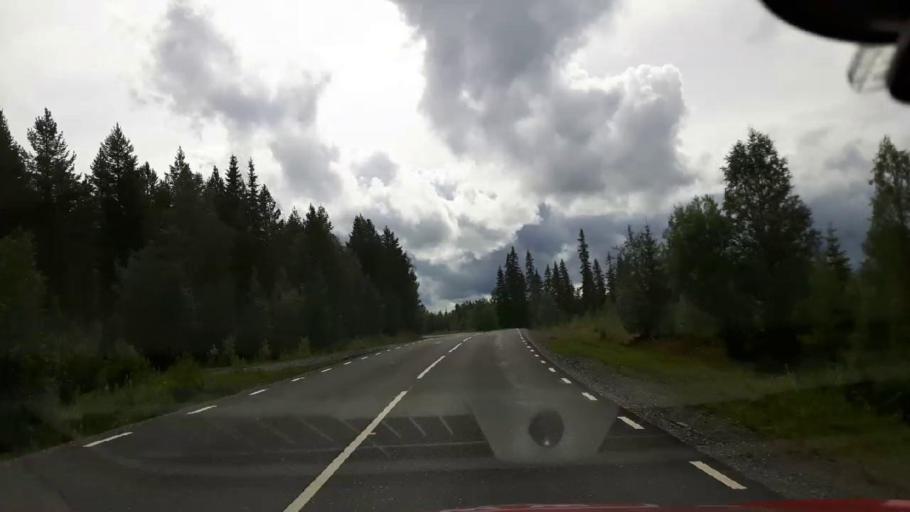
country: NO
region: Nord-Trondelag
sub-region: Lierne
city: Sandvika
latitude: 64.6074
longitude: 14.1198
